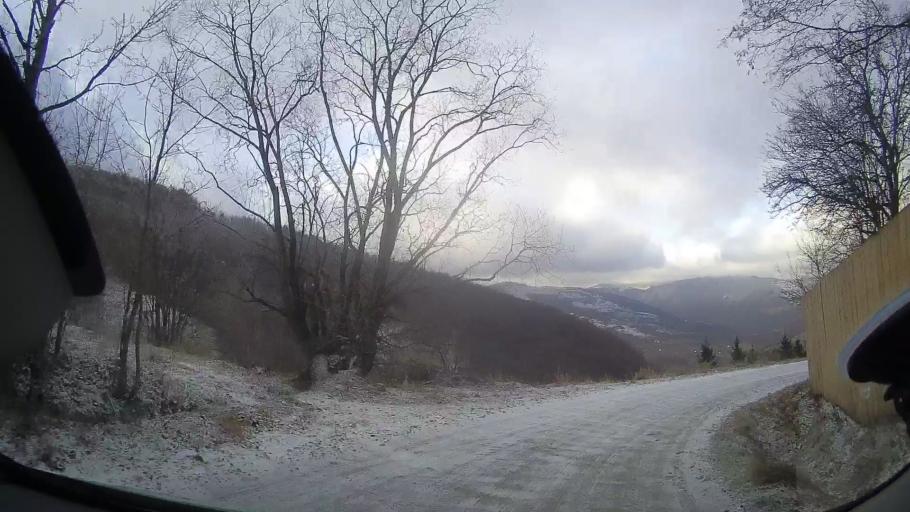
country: RO
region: Cluj
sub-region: Comuna Valea Ierii
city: Valea Ierii
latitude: 46.6652
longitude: 23.3326
